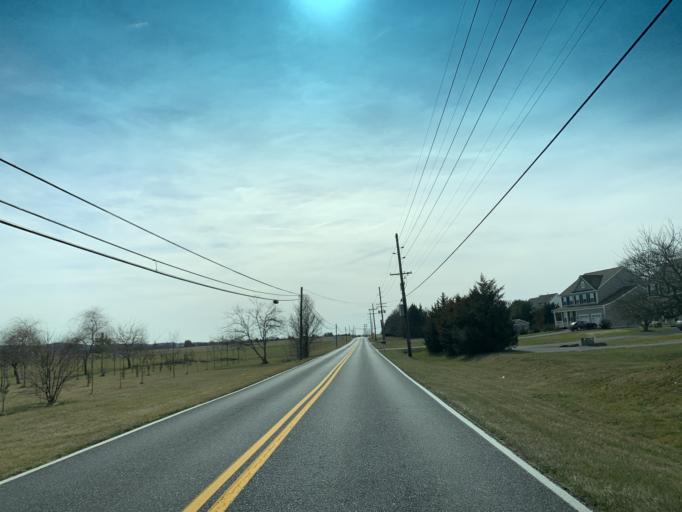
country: US
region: Maryland
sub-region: Frederick County
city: Adamstown
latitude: 39.3059
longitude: -77.4628
